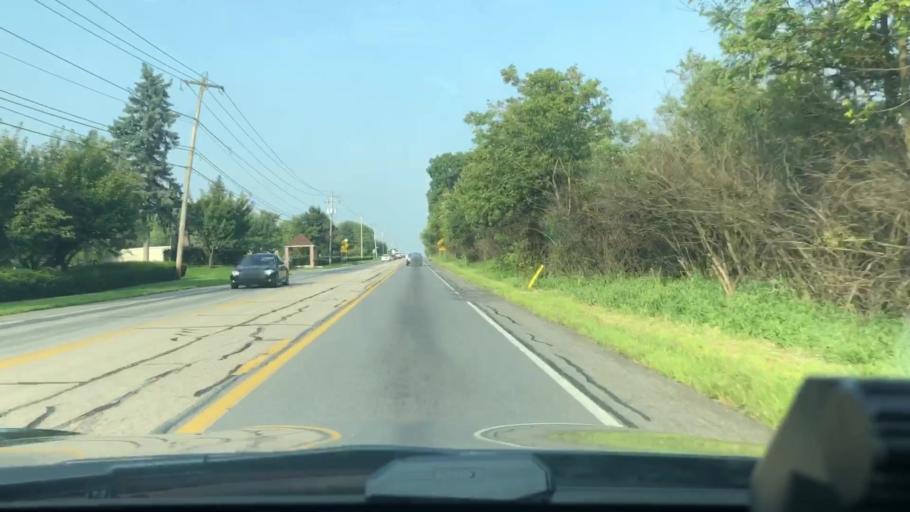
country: US
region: Pennsylvania
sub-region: Berks County
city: Blandon
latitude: 40.4568
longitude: -75.8826
